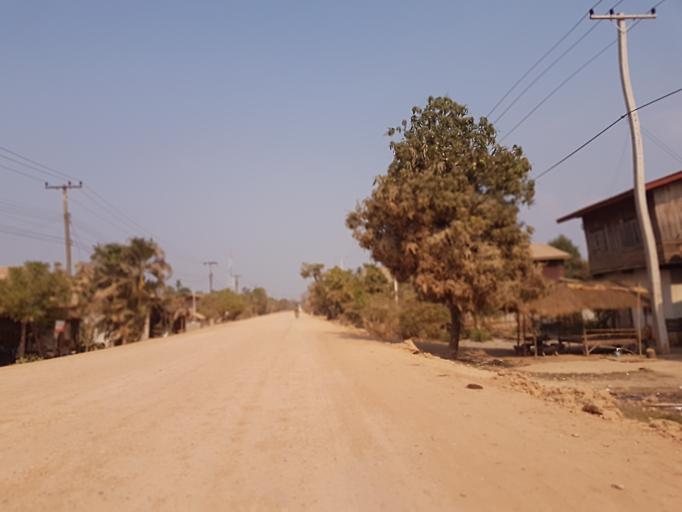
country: TH
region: Nong Khai
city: Nong Khai
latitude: 17.9410
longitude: 102.7957
